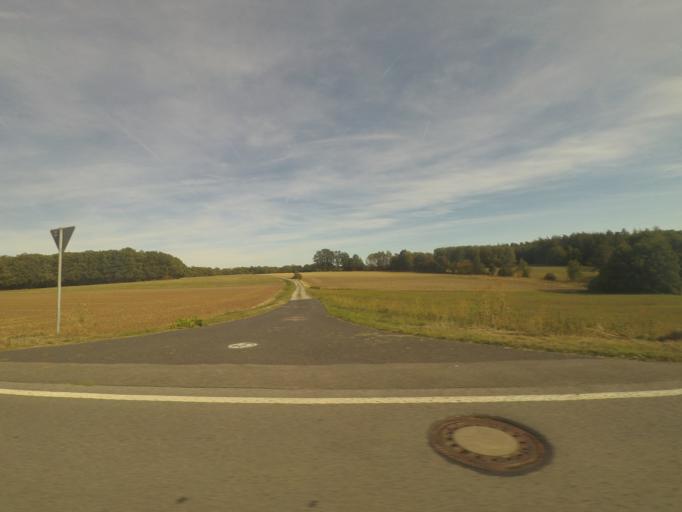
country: DE
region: Bavaria
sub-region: Regierungsbezirk Unterfranken
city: Fladungen
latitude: 50.5333
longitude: 10.1589
